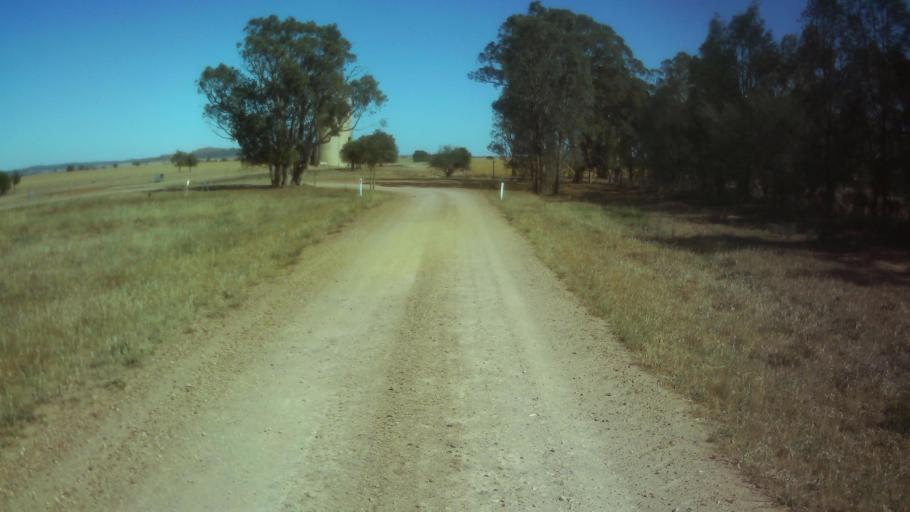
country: AU
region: New South Wales
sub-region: Weddin
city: Grenfell
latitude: -33.9914
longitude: 148.3406
